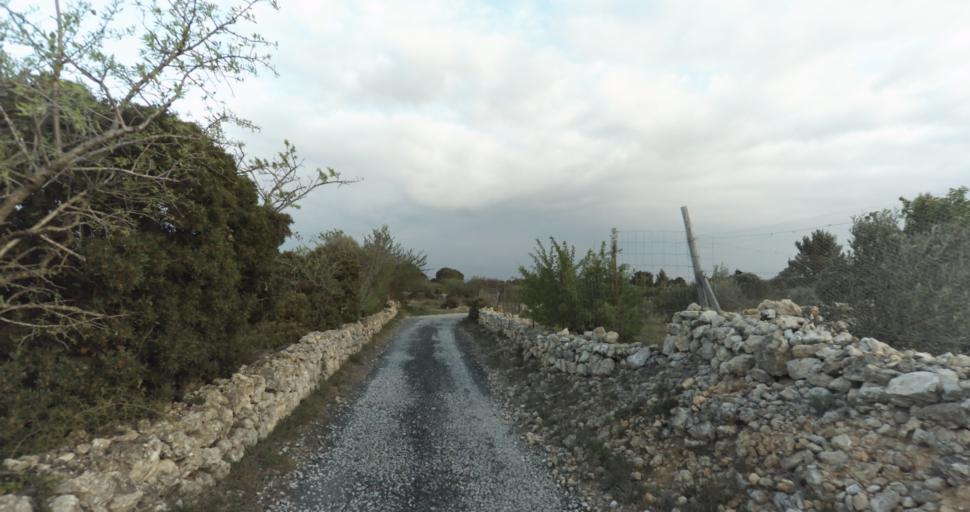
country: FR
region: Languedoc-Roussillon
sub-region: Departement de l'Aude
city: Leucate
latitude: 42.9229
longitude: 3.0197
